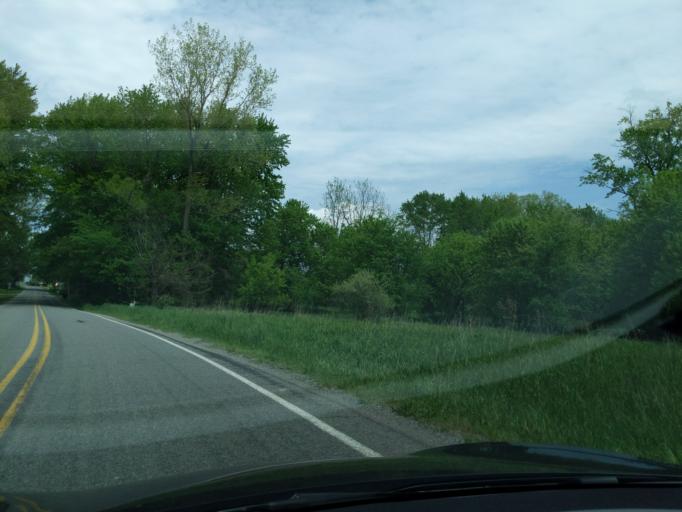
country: US
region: Michigan
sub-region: Ingham County
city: Stockbridge
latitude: 42.4648
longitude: -84.1611
